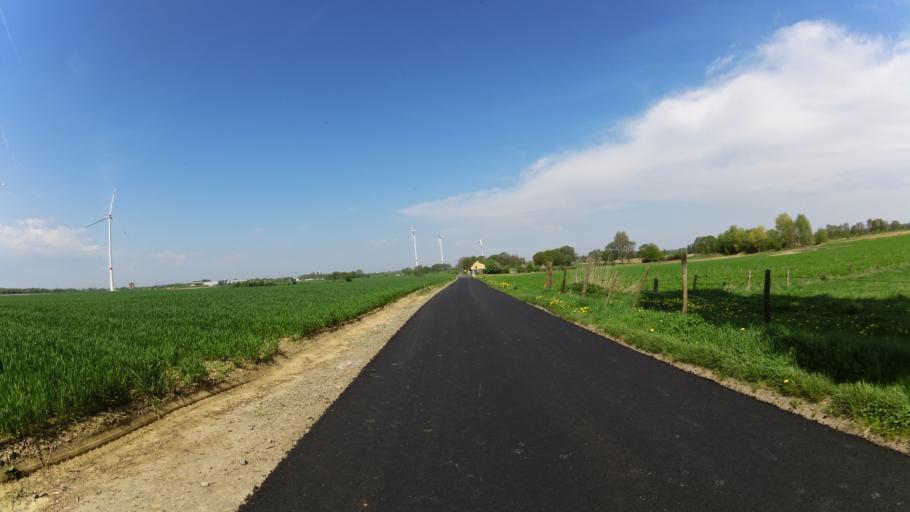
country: NL
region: Limburg
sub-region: Gemeente Kerkrade
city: Kerkrade
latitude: 50.8230
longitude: 6.0378
